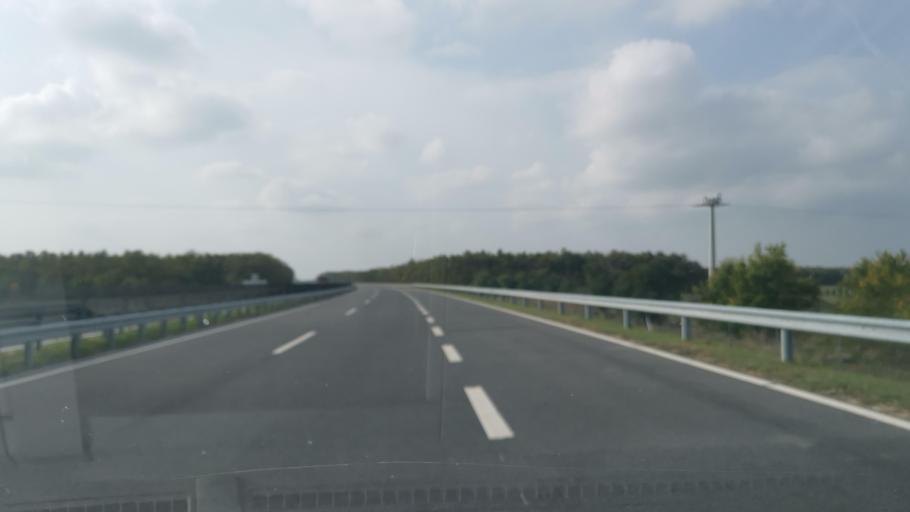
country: HU
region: Gyor-Moson-Sopron
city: Fertoszentmiklos
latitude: 47.5859
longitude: 16.9343
